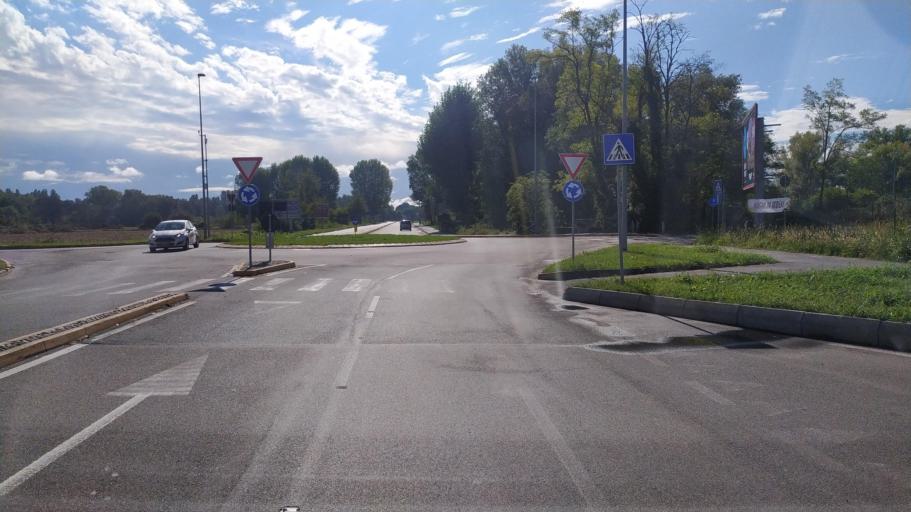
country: IT
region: Lombardy
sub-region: Citta metropolitana di Milano
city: Cusago
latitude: 45.4361
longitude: 9.0472
